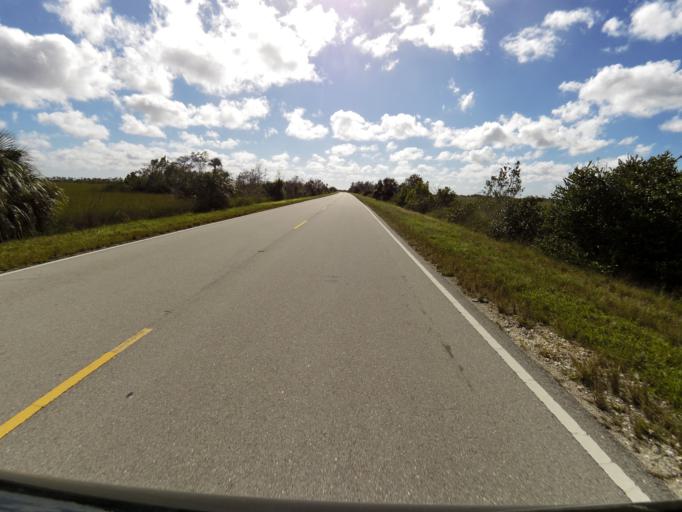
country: US
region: Florida
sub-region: Miami-Dade County
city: Florida City
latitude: 25.3725
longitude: -80.8160
